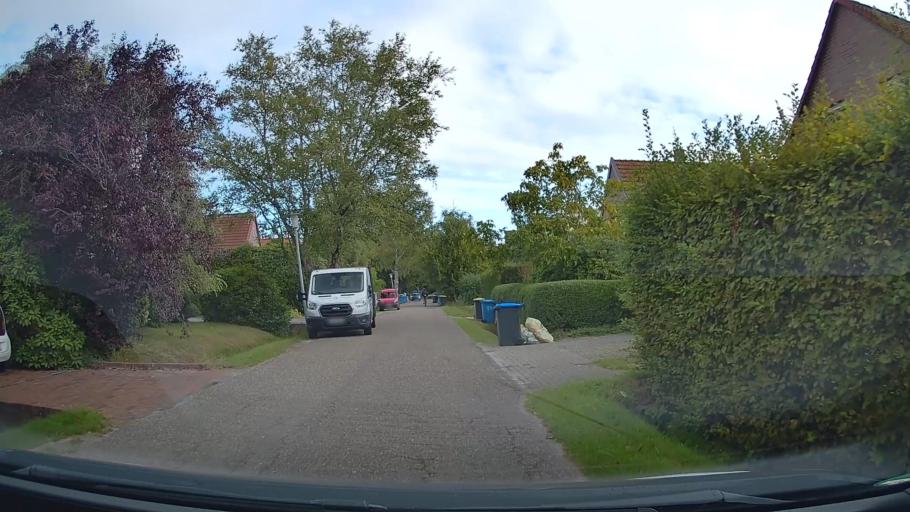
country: DE
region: Lower Saxony
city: Oldenburg
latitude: 53.1506
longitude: 8.1708
